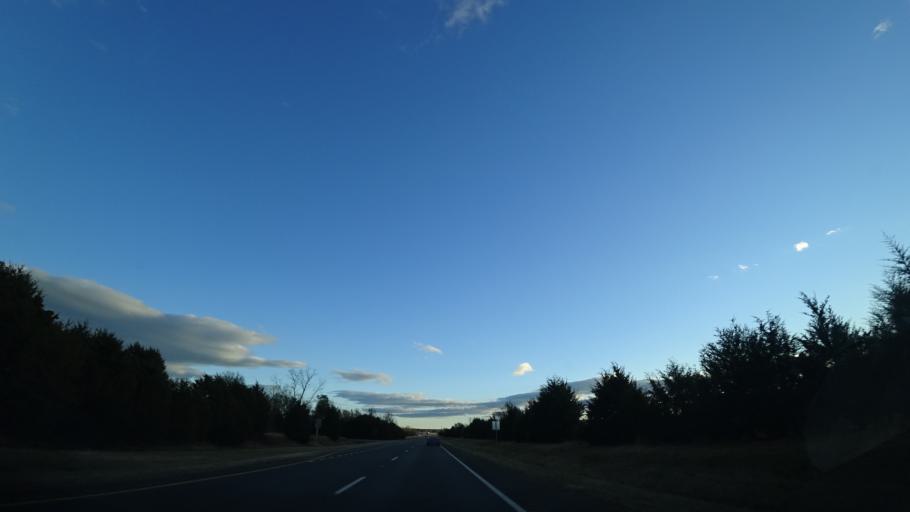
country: US
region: Virginia
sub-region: Fauquier County
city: Bealeton
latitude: 38.5505
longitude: -77.7328
